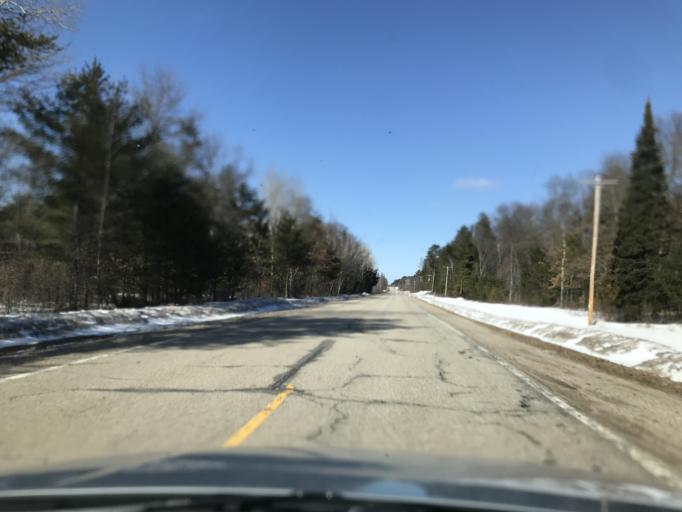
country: US
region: Wisconsin
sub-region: Marinette County
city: Niagara
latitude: 45.3650
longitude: -88.1005
